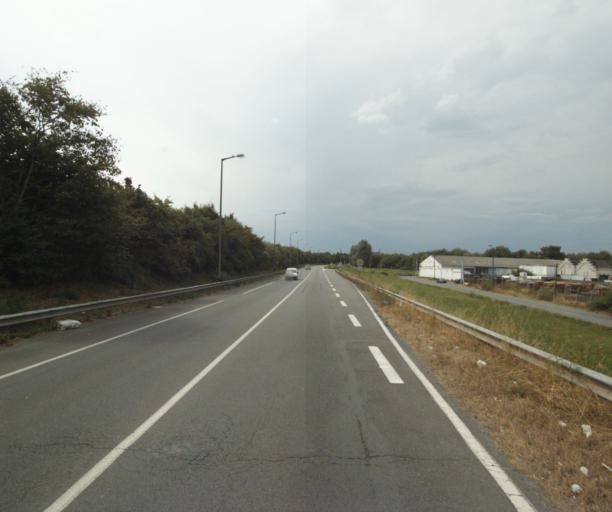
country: FR
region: Nord-Pas-de-Calais
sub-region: Departement du Nord
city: Wattrelos
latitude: 50.6872
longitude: 3.2224
